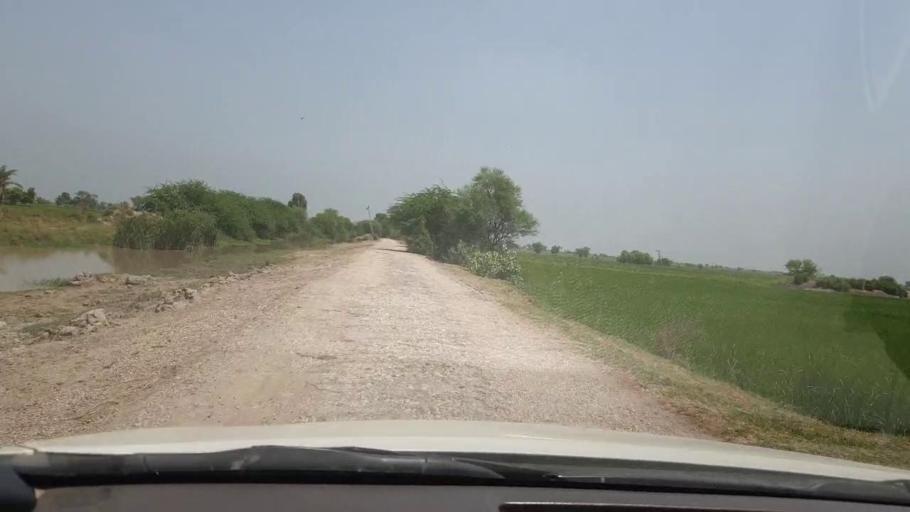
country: PK
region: Sindh
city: Garhi Yasin
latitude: 27.8956
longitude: 68.5430
